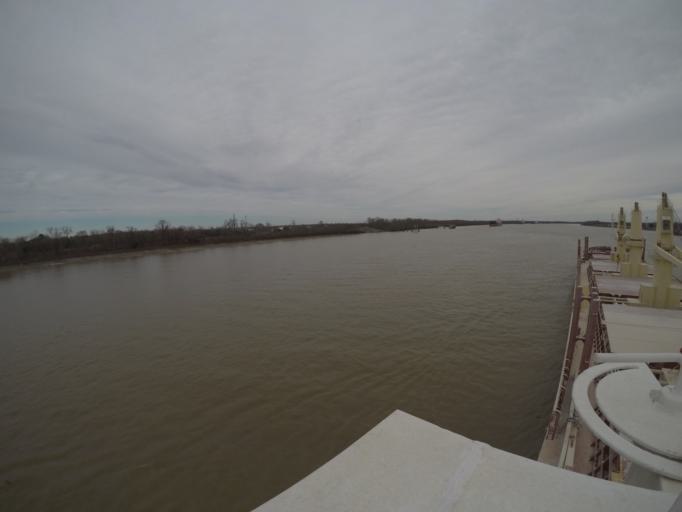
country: US
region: Louisiana
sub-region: Saint John the Baptist Parish
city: Reserve
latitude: 30.0469
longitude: -90.5272
